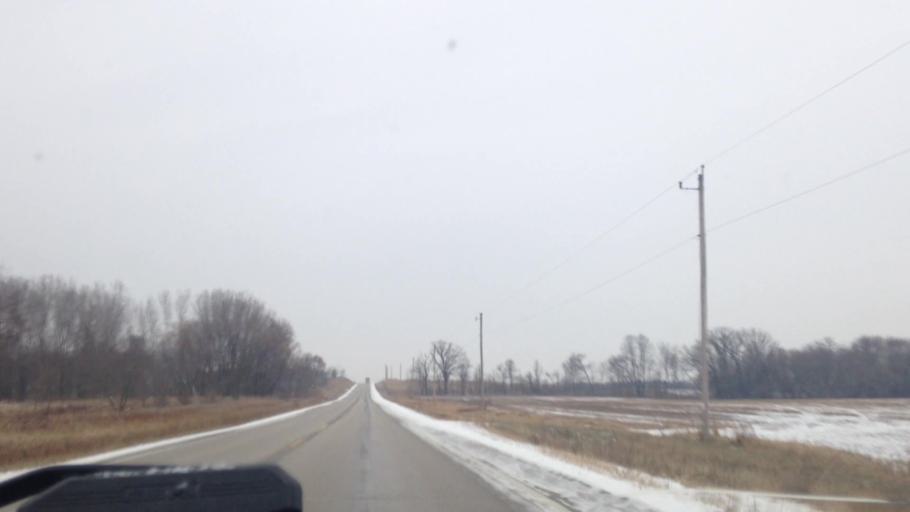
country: US
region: Wisconsin
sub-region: Dodge County
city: Hustisford
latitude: 43.3916
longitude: -88.5417
